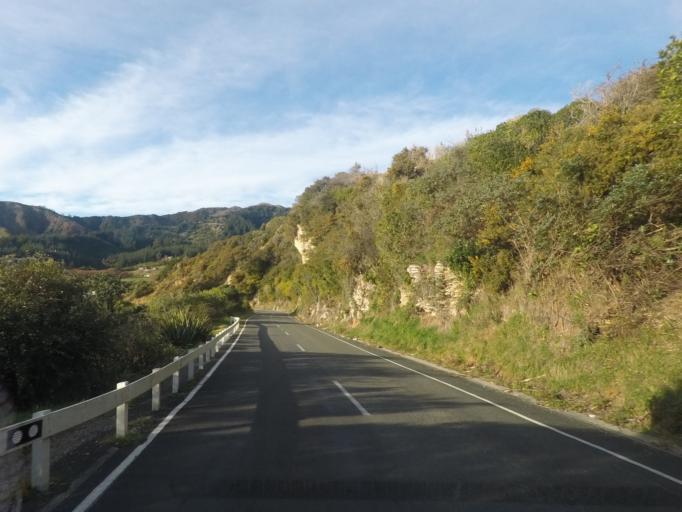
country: NZ
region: Tasman
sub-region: Tasman District
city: Takaka
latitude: -40.8223
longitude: 172.9029
